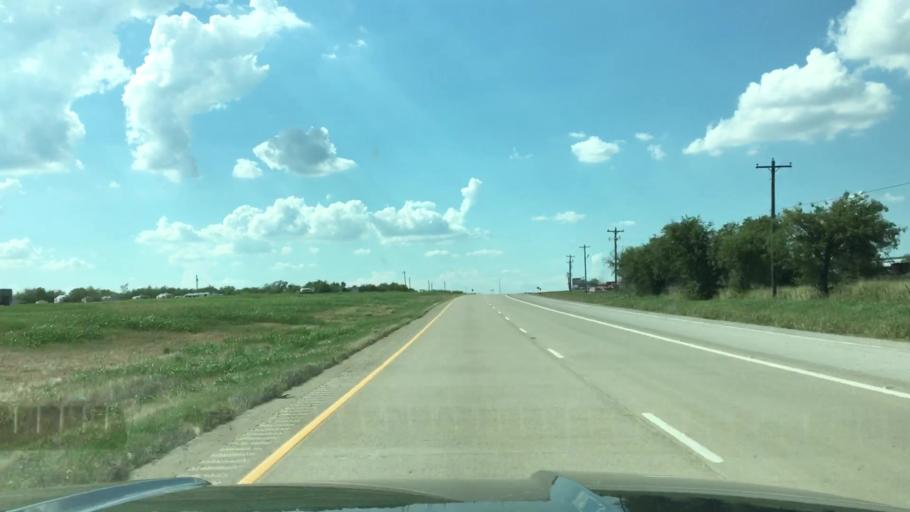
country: US
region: Texas
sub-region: Wise County
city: Rhome
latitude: 33.0413
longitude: -97.4477
